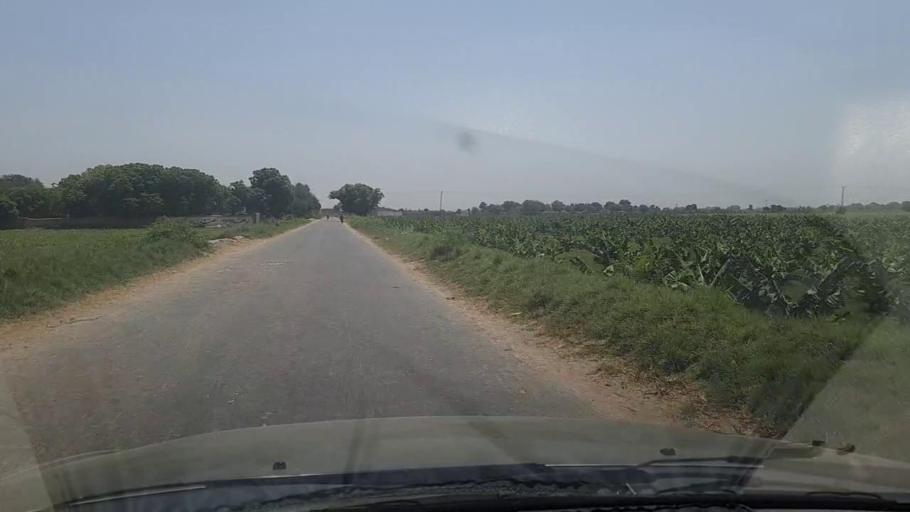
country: PK
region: Sindh
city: Chambar
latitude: 25.2676
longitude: 68.6402
